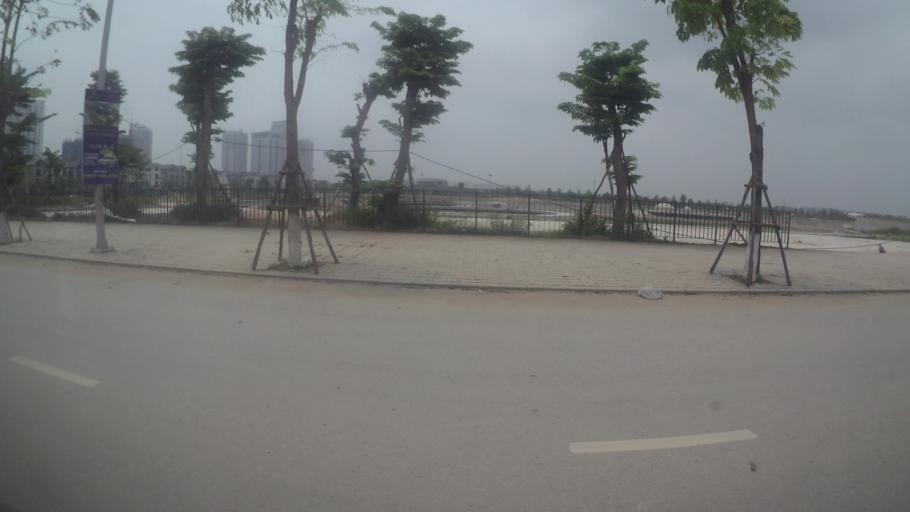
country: VN
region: Ha Noi
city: Ha Dong
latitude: 20.9811
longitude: 105.7595
